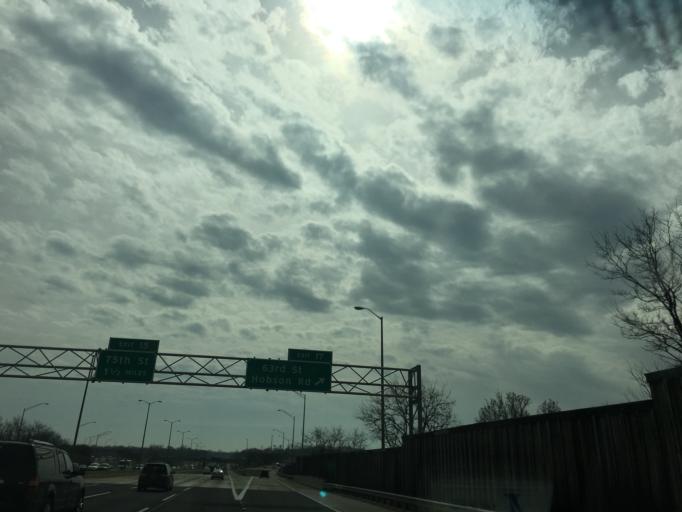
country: US
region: Illinois
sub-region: DuPage County
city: Woodridge
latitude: 41.7760
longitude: -88.0497
